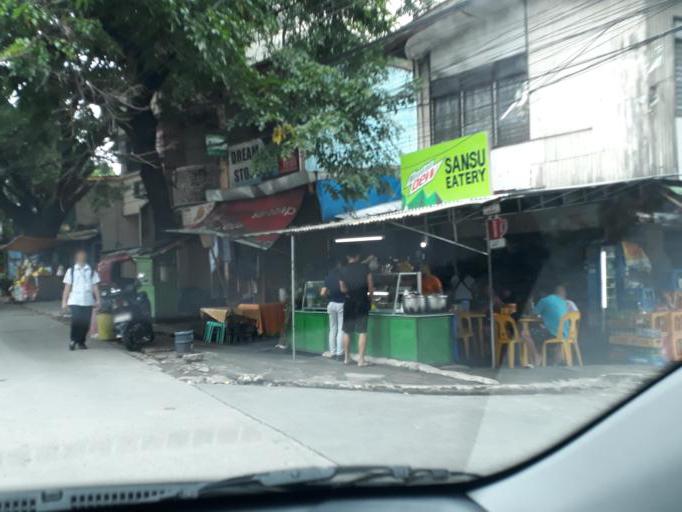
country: PH
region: Calabarzon
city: Del Monte
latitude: 14.6278
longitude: 121.0249
